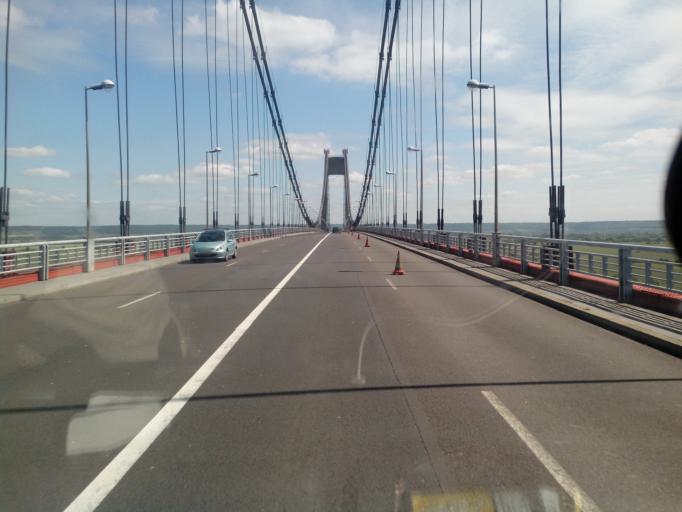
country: FR
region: Haute-Normandie
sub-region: Departement de la Seine-Maritime
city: Tancarville
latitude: 49.4745
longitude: 0.4624
